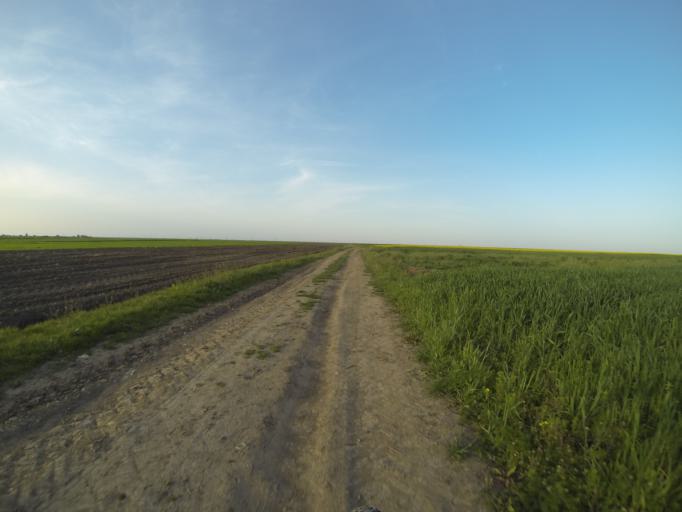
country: RO
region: Dolj
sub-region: Comuna Pielesti
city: Pielesti
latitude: 44.3370
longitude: 23.8997
